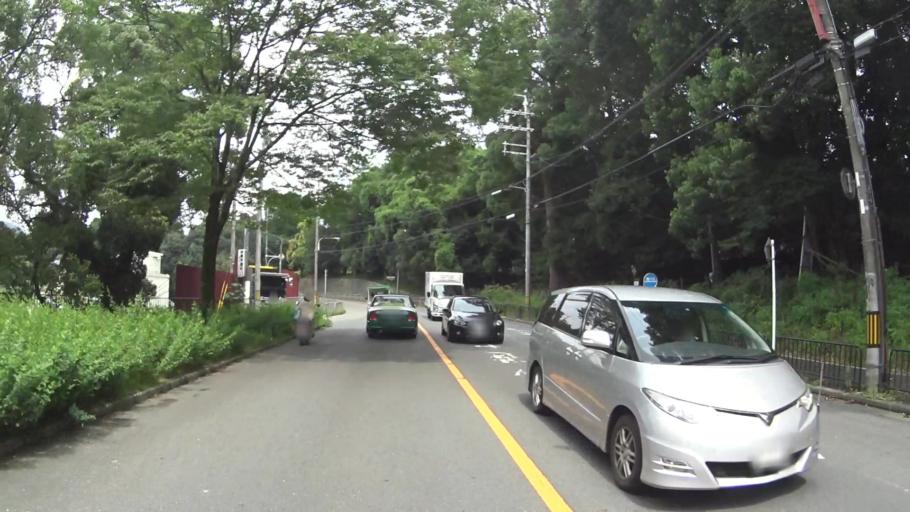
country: JP
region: Kyoto
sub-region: Kyoto-shi
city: Kamigyo-ku
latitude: 35.0647
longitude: 135.7504
